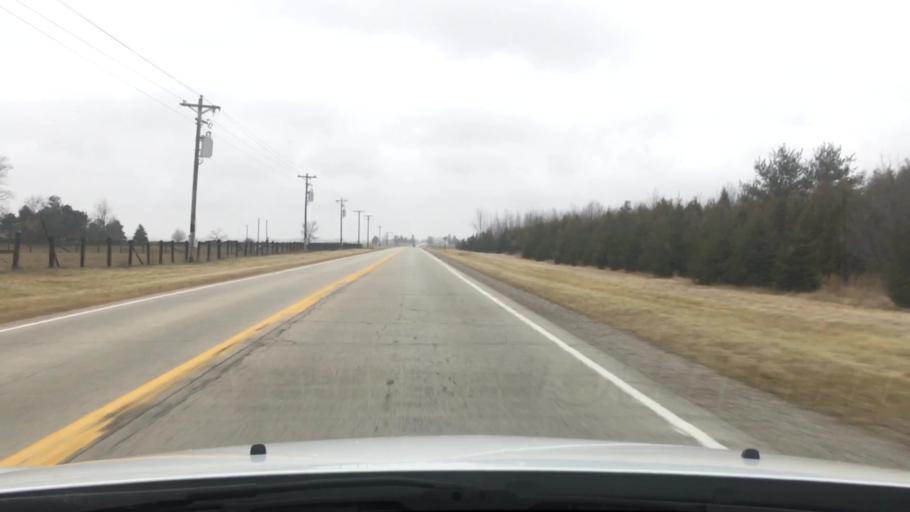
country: US
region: Illinois
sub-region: Iroquois County
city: Watseka
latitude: 40.8907
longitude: -87.6889
